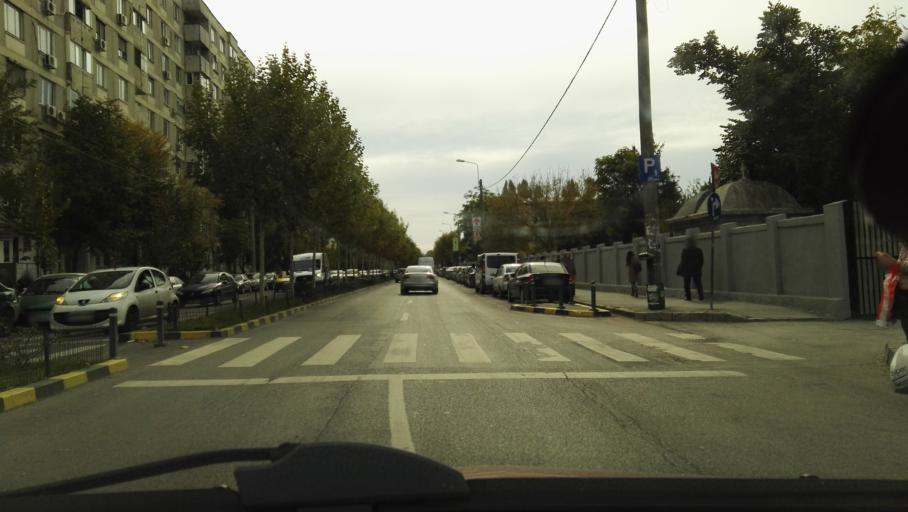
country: RO
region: Bucuresti
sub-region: Municipiul Bucuresti
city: Bucharest
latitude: 44.3919
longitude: 26.1232
